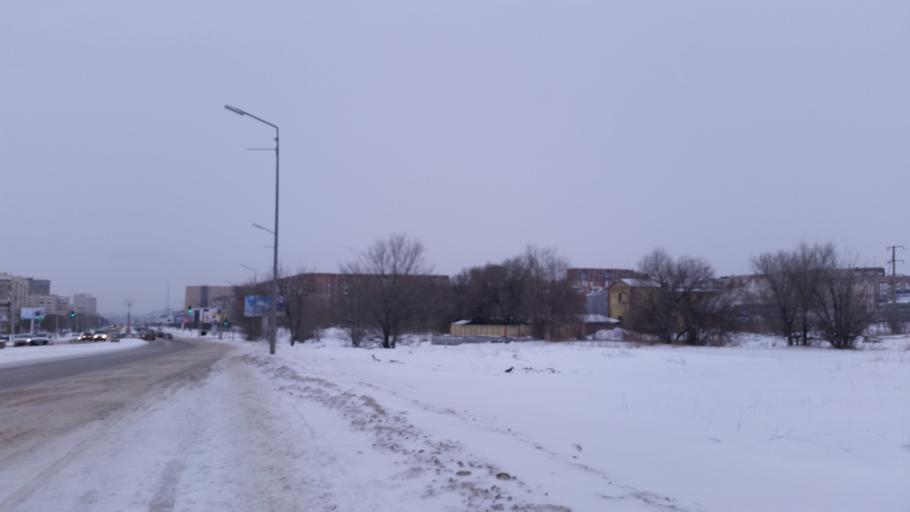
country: KZ
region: Qaraghandy
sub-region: Qaraghandy Qalasy
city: Karagandy
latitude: 49.7762
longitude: 73.1551
